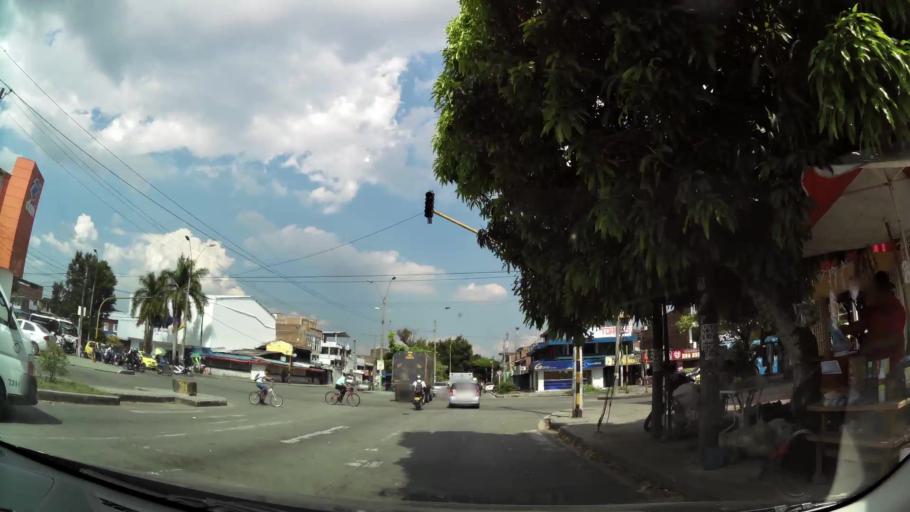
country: CO
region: Valle del Cauca
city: Cali
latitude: 3.4194
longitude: -76.5178
